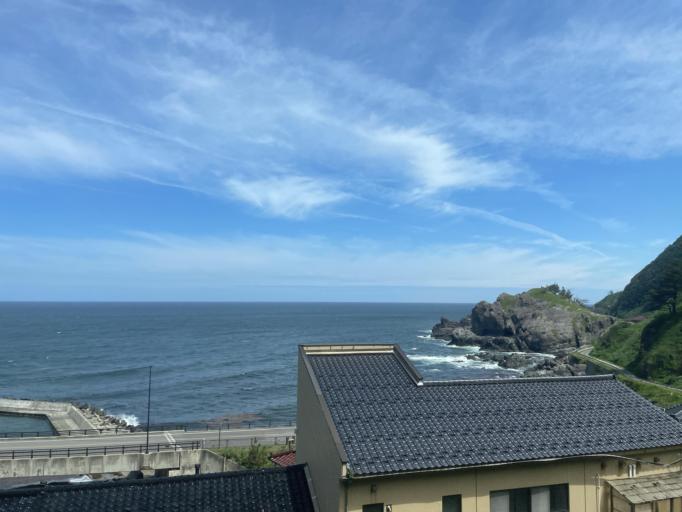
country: JP
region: Yamagata
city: Tsuruoka
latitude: 38.7035
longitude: 139.6606
